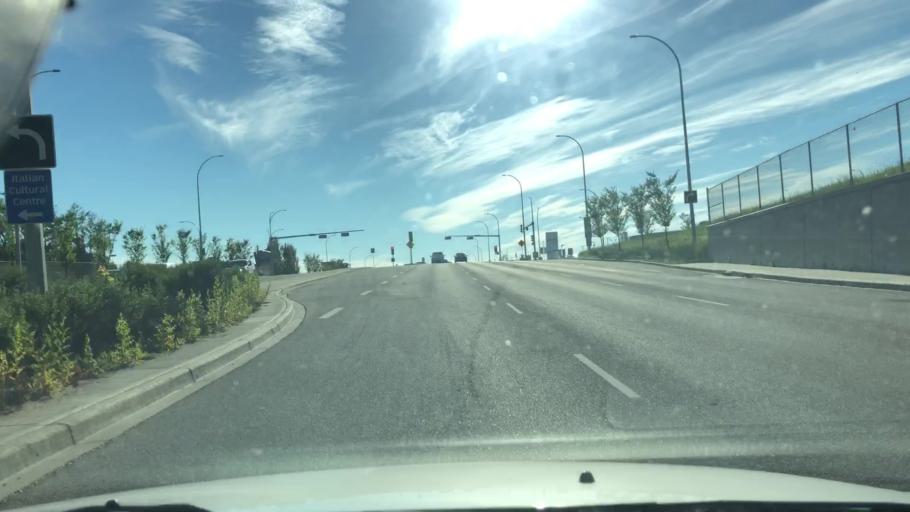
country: CA
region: Alberta
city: St. Albert
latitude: 53.5995
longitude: -113.5664
